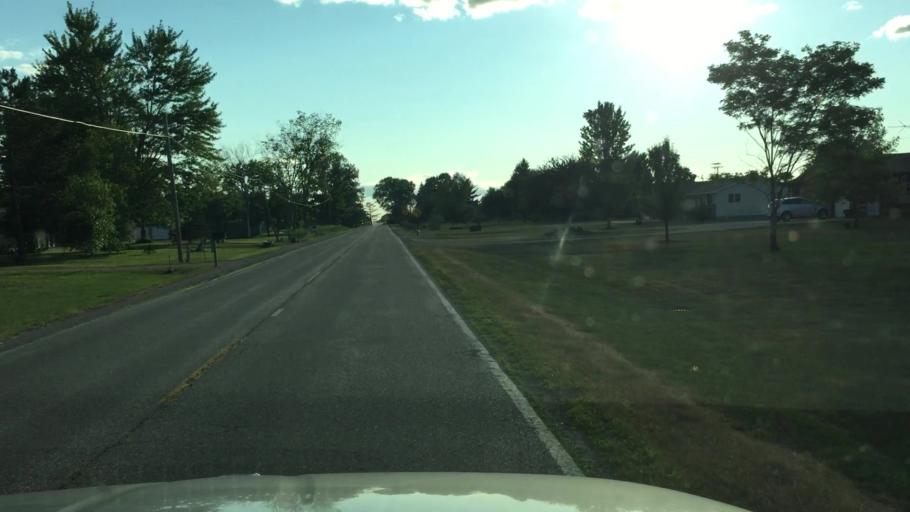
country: US
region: Michigan
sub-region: Saint Clair County
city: Capac
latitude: 43.0271
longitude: -82.9336
